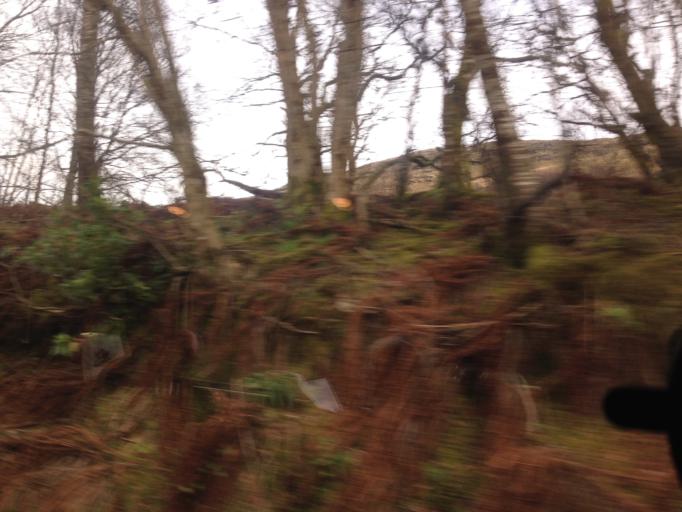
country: GB
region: Scotland
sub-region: Argyll and Bute
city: Garelochhead
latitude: 56.1974
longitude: -4.7332
